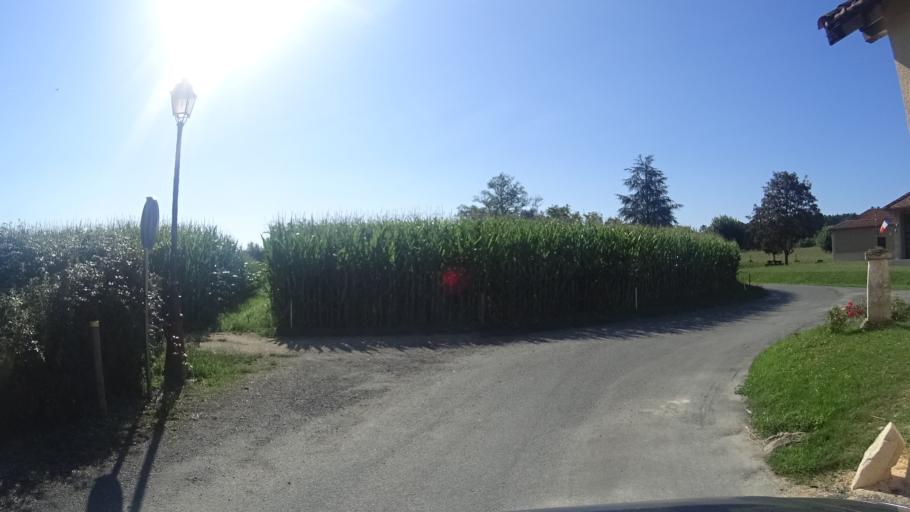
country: FR
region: Aquitaine
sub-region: Departement de la Dordogne
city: Sourzac
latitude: 45.0163
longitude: 0.4030
